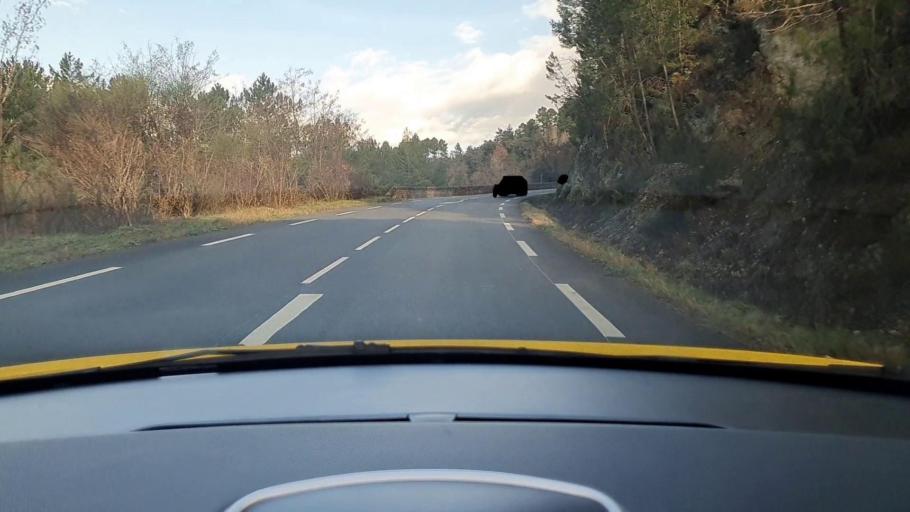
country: FR
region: Languedoc-Roussillon
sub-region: Departement du Gard
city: Branoux-les-Taillades
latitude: 44.3264
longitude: 3.9673
